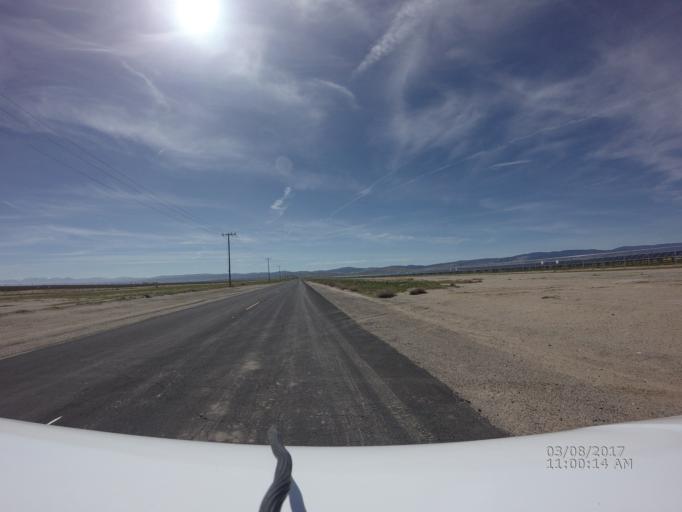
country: US
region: California
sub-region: Los Angeles County
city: Green Valley
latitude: 34.8188
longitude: -118.3792
